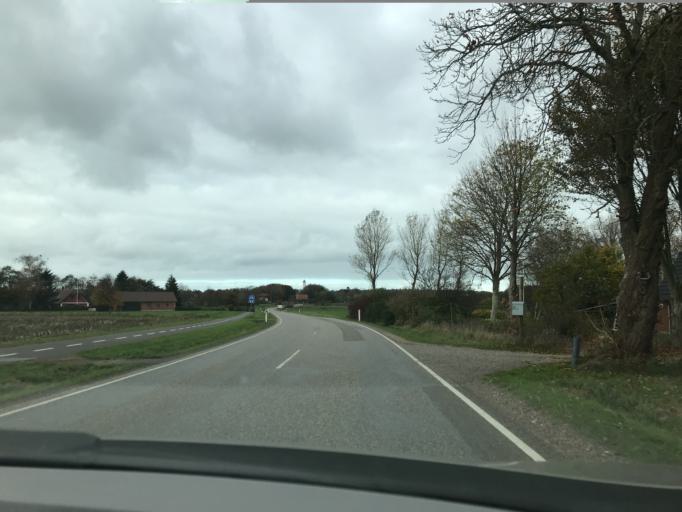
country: DK
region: South Denmark
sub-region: Varde Kommune
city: Olgod
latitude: 55.8012
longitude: 8.6369
